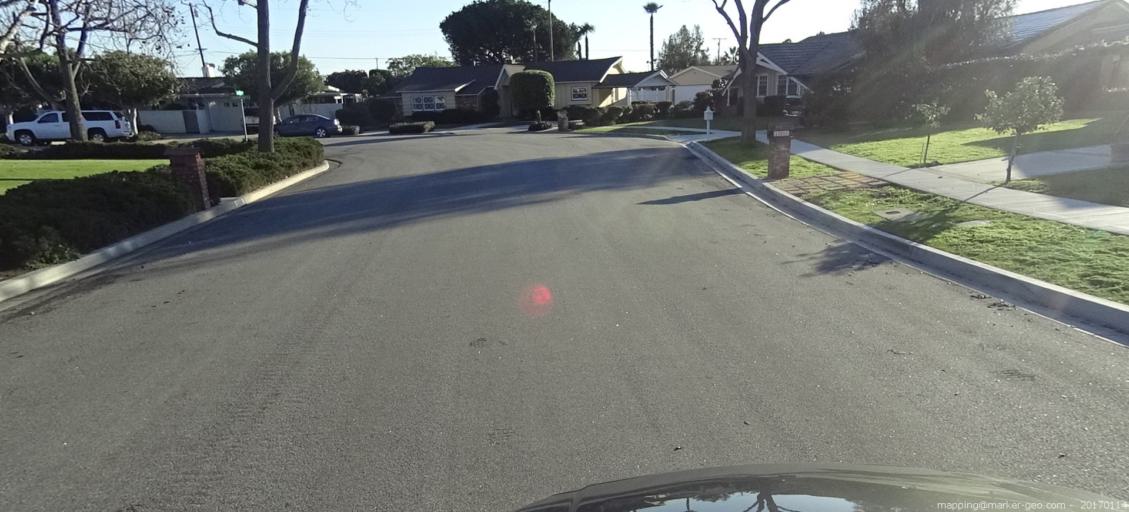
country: US
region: California
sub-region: Orange County
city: Tustin
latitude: 33.7659
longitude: -117.8222
